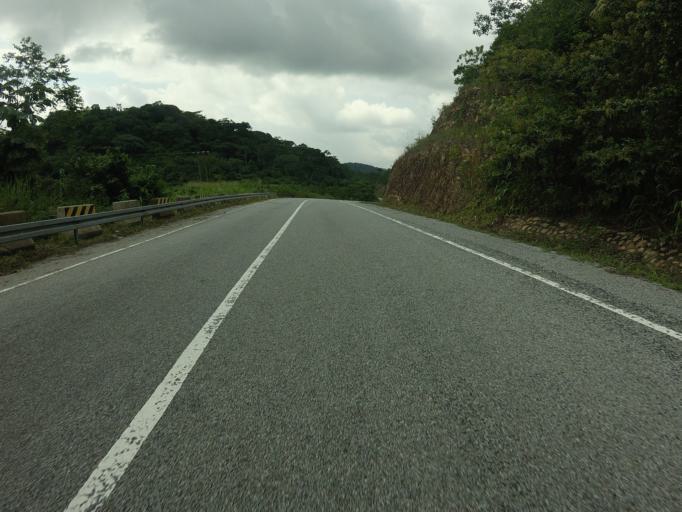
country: GH
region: Volta
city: Kpandu
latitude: 6.8310
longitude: 0.4179
